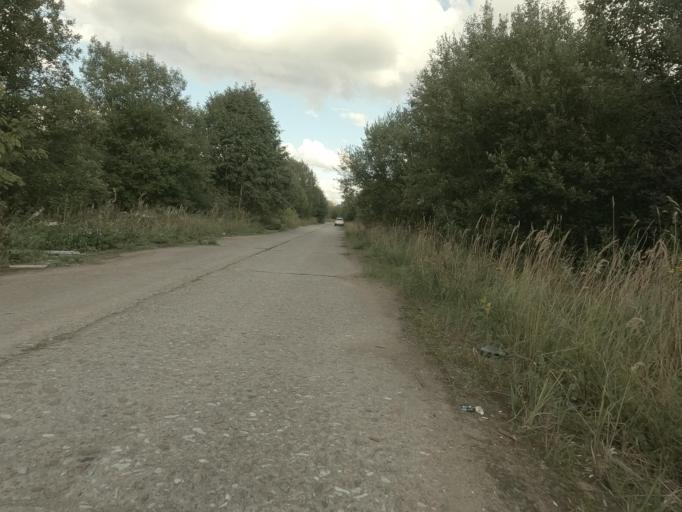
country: RU
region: Leningrad
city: Mga
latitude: 59.7489
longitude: 31.0939
